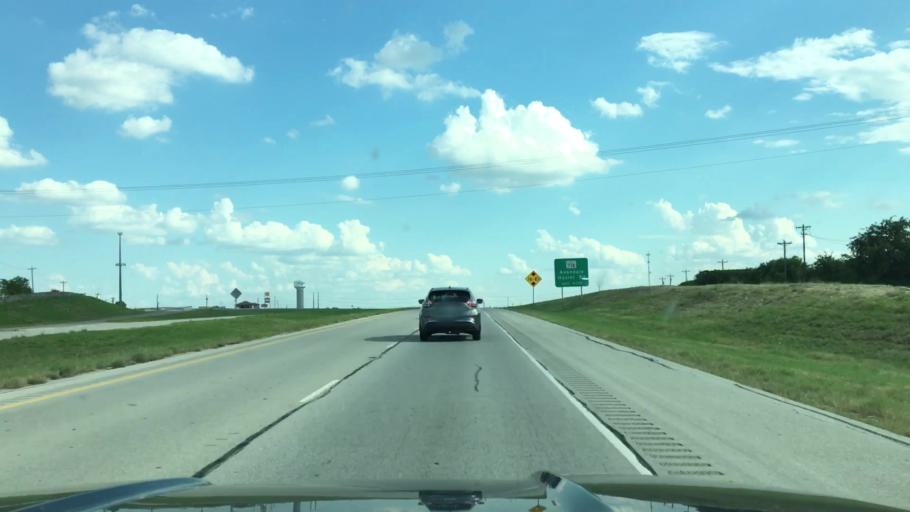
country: US
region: Texas
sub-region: Tarrant County
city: Pecan Acres
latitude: 32.9761
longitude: -97.4235
